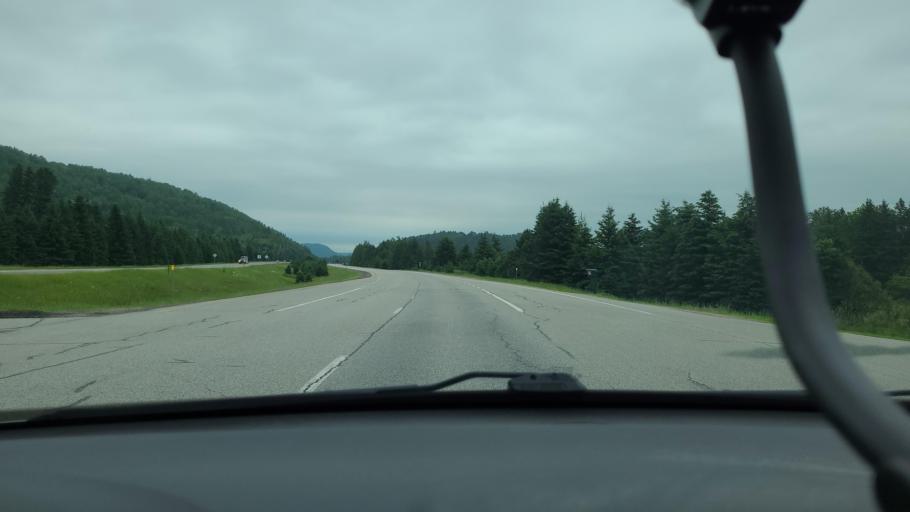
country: CA
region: Quebec
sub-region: Laurentides
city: Labelle
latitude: 46.2037
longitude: -74.7178
